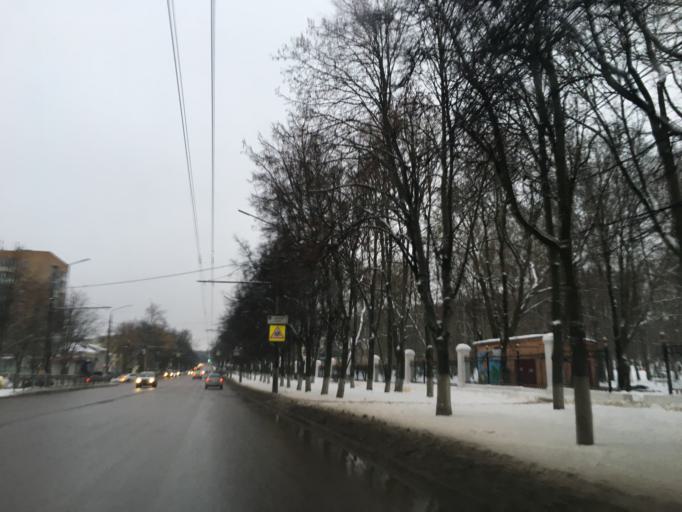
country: RU
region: Tula
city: Tula
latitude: 54.1862
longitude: 37.5913
